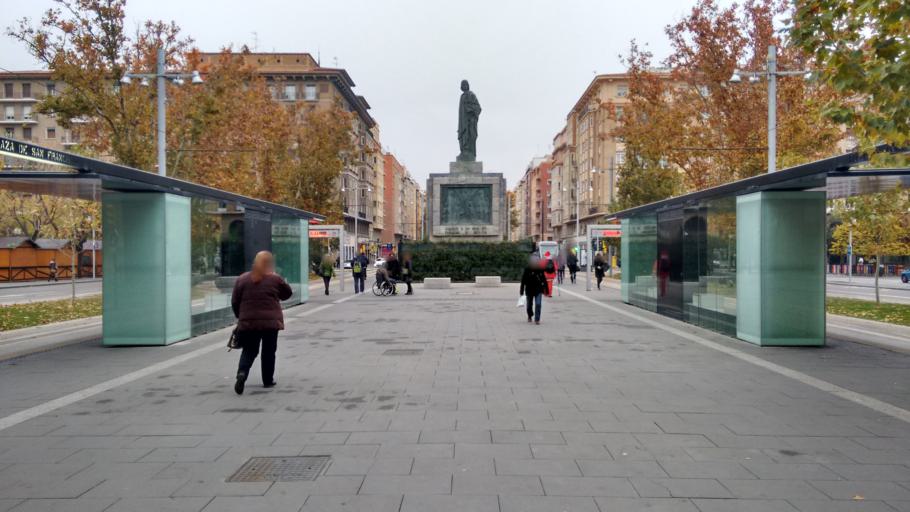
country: ES
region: Aragon
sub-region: Provincia de Zaragoza
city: Delicias
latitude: 41.6406
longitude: -0.8952
